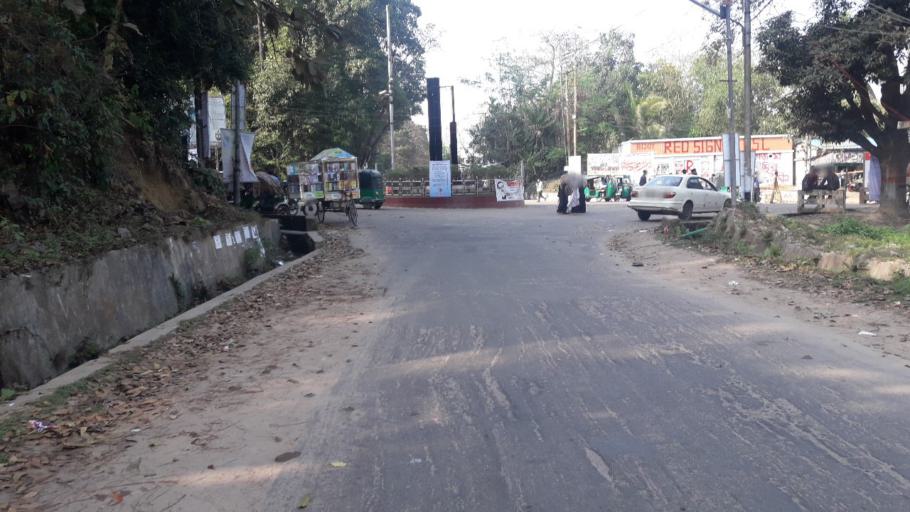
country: BD
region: Chittagong
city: Chittagong
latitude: 22.4707
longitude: 91.7934
